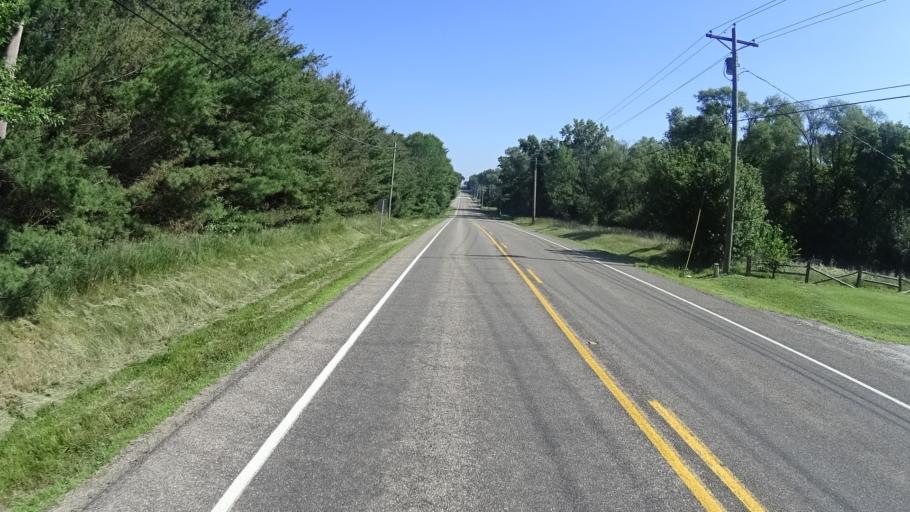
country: US
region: Indiana
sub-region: Hancock County
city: Fortville
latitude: 39.9616
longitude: -85.8432
